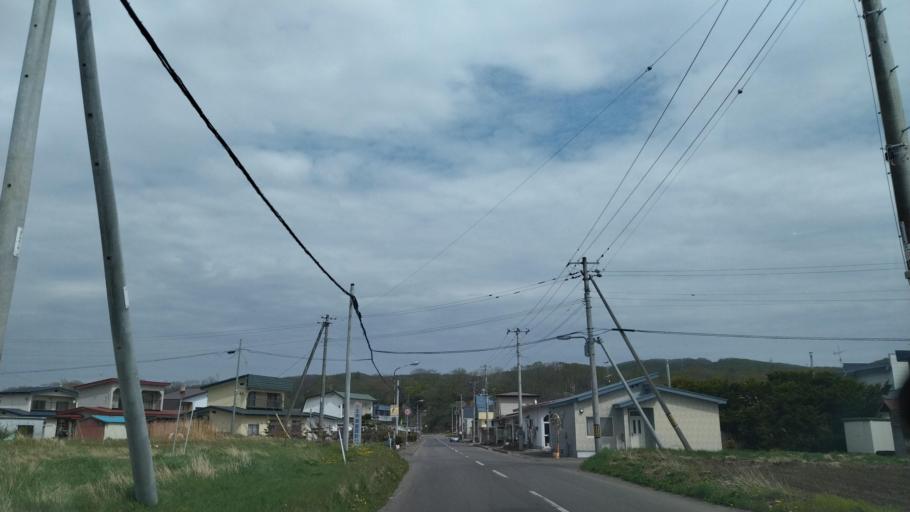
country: JP
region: Hokkaido
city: Otofuke
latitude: 43.2366
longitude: 143.5559
